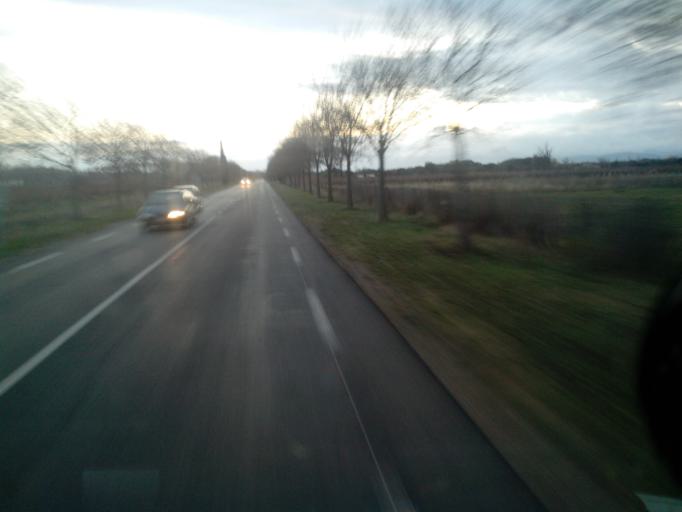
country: FR
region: Languedoc-Roussillon
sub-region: Departement de l'Herault
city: Aniane
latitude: 43.6767
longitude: 3.5746
